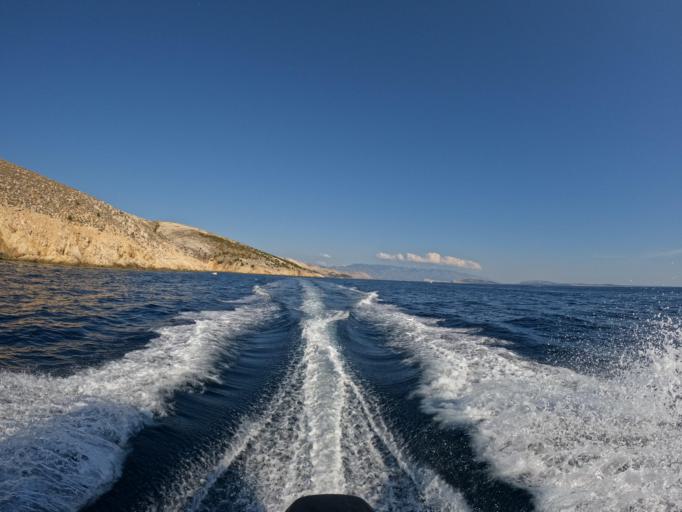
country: HR
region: Primorsko-Goranska
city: Punat
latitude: 44.9682
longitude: 14.6434
